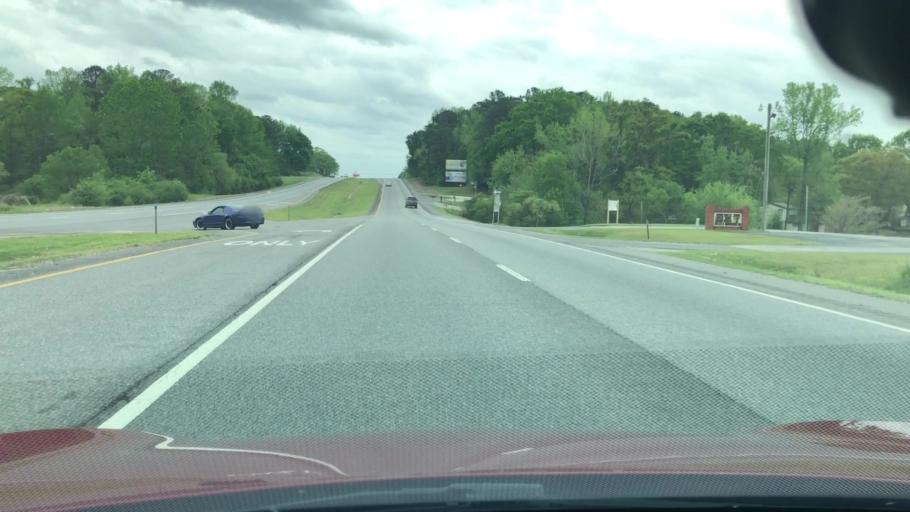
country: US
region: Alabama
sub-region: Tallapoosa County
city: Alexander City
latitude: 32.9475
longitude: -85.9850
